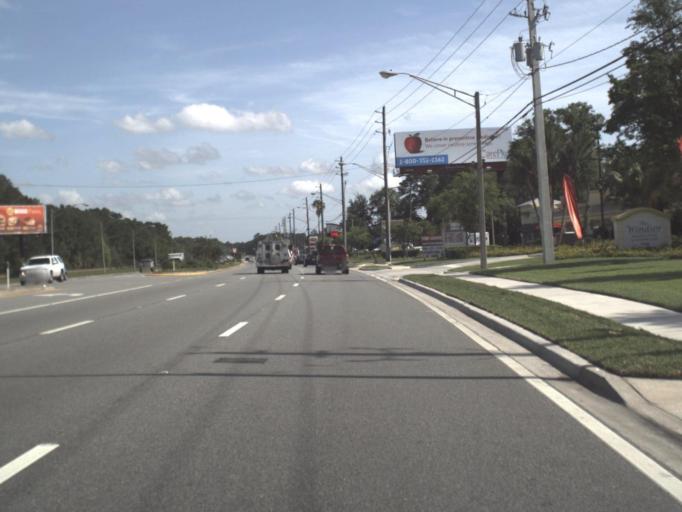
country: US
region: Florida
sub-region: Clay County
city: Orange Park
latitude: 30.2418
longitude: -81.6963
